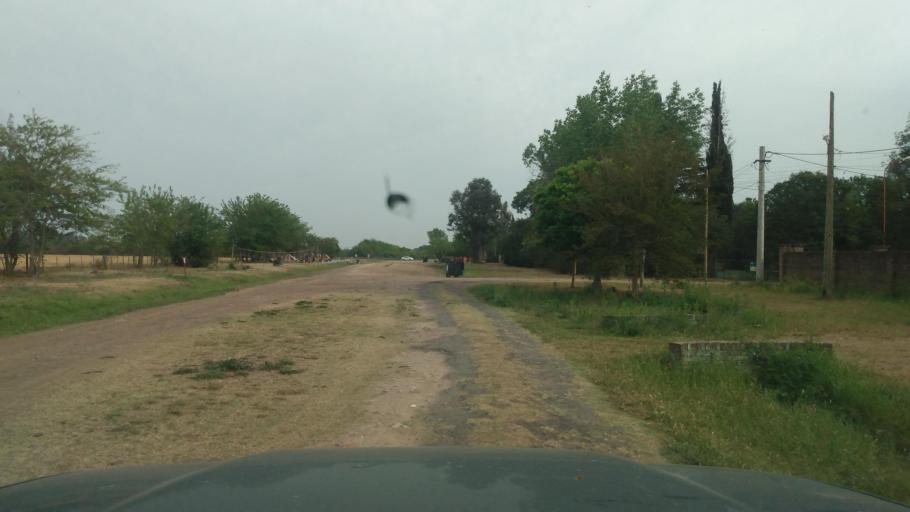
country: AR
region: Buenos Aires
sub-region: Partido de Lujan
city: Lujan
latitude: -34.5453
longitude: -59.1453
